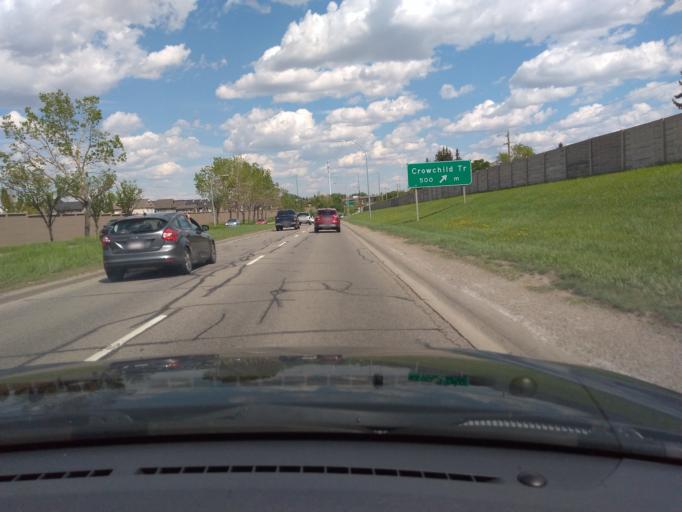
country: CA
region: Alberta
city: Calgary
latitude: 51.0010
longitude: -114.1262
